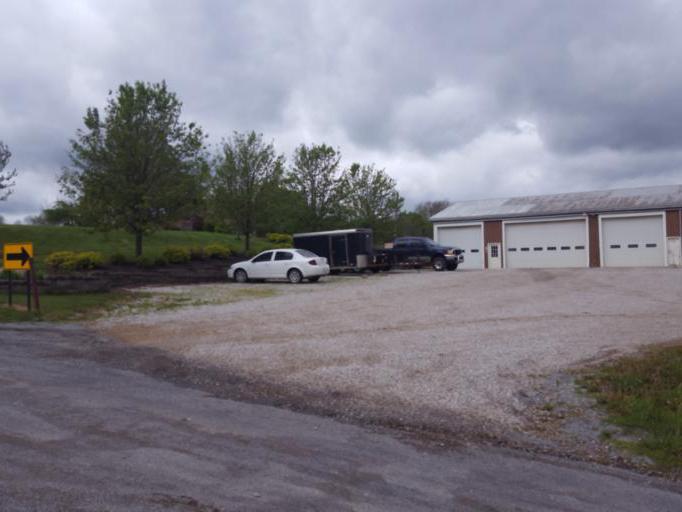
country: US
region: Ohio
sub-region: Knox County
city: Danville
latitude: 40.5388
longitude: -82.3329
